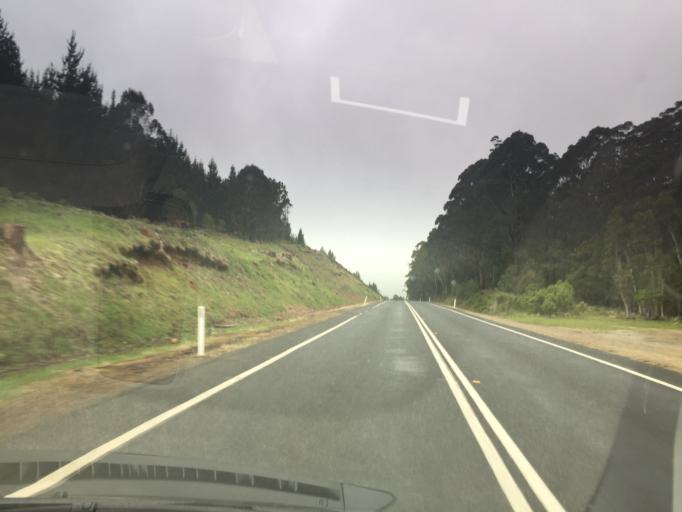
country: AU
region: New South Wales
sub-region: Bombala
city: Bombala
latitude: -36.6135
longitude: 149.3720
